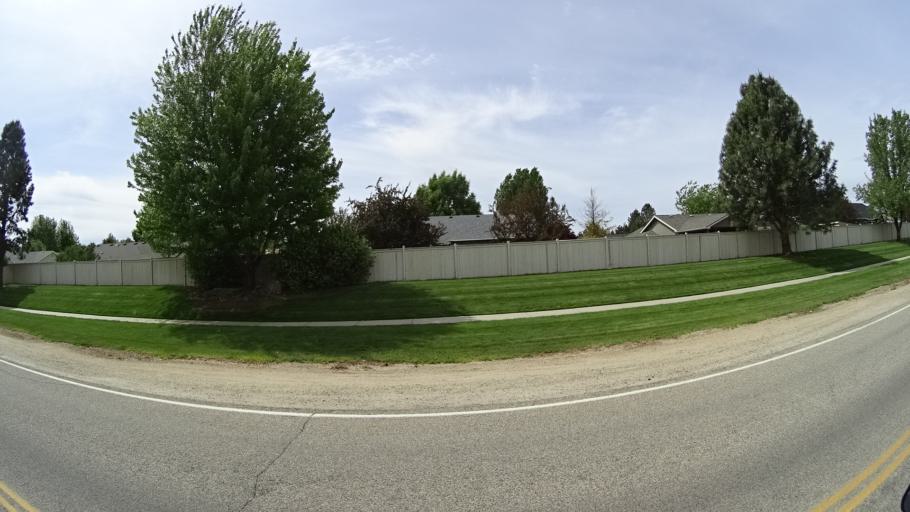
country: US
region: Idaho
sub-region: Ada County
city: Meridian
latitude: 43.5539
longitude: -116.3320
